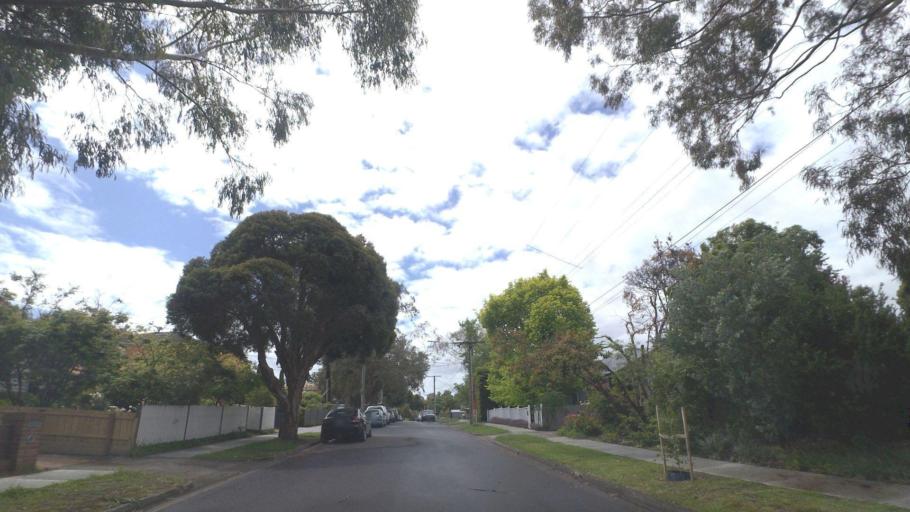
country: AU
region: Victoria
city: Mitcham
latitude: -37.8217
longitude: 145.1978
